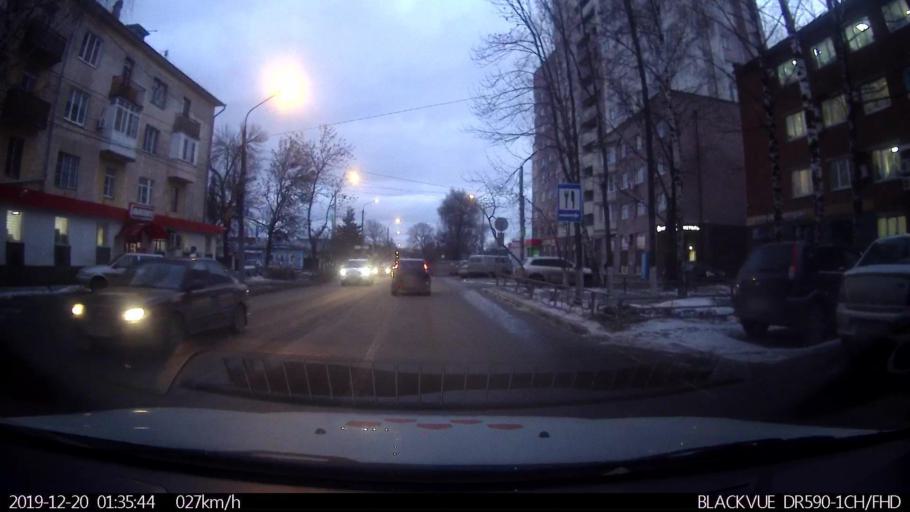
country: RU
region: Nizjnij Novgorod
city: Nizhniy Novgorod
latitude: 56.3112
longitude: 44.0368
